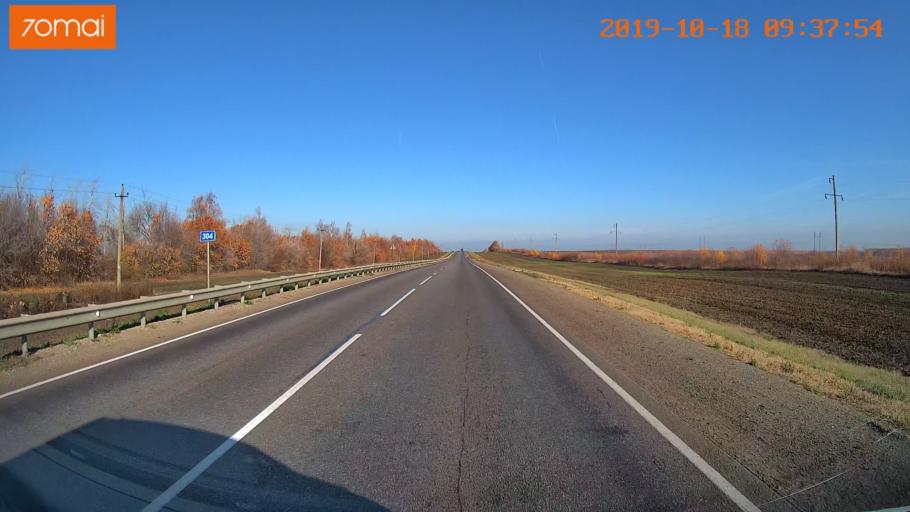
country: RU
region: Tula
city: Yefremov
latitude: 53.2298
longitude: 38.1391
